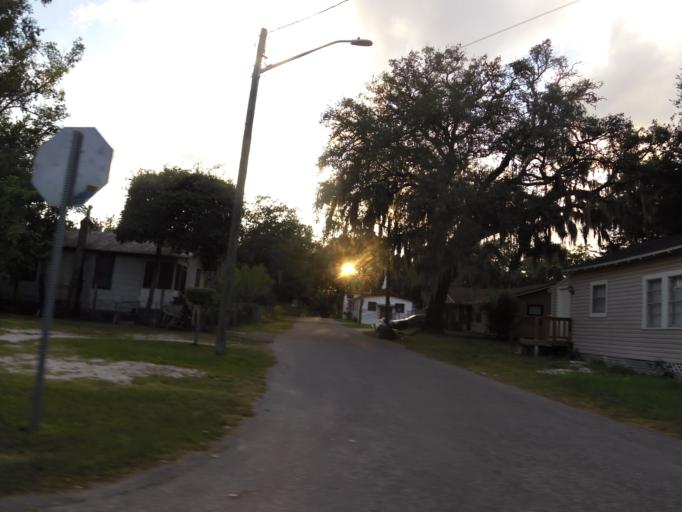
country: US
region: Florida
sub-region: Duval County
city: Jacksonville
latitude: 30.3255
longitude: -81.6891
